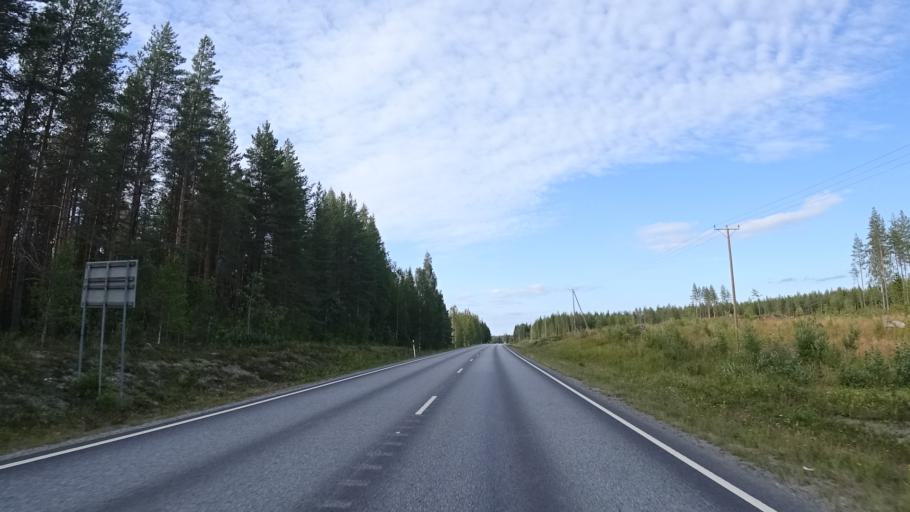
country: FI
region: North Karelia
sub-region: Joensuu
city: Eno
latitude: 62.8574
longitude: 30.1951
